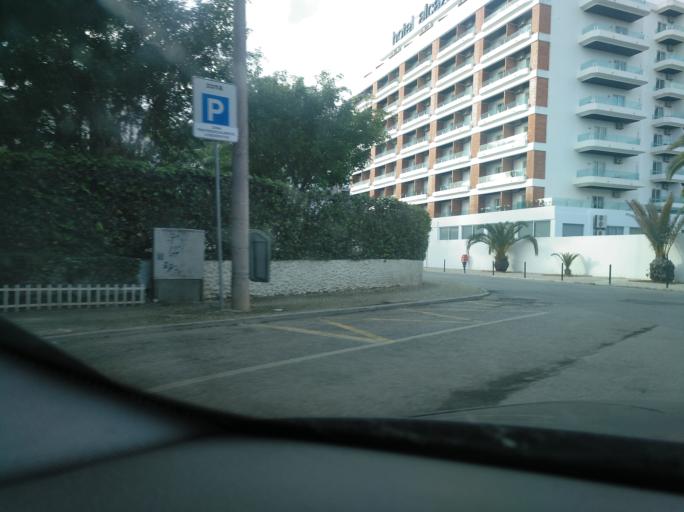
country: PT
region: Faro
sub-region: Vila Real de Santo Antonio
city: Monte Gordo
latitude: 37.1807
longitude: -7.4451
